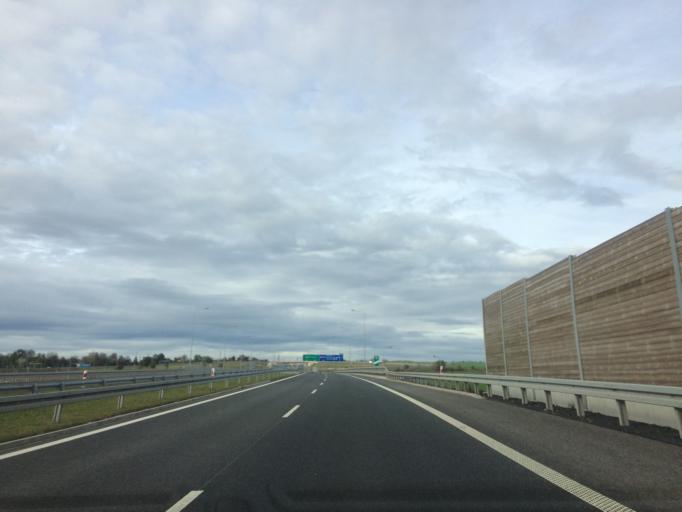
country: PL
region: Lower Silesian Voivodeship
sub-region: Legnica
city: Legnica
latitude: 51.1666
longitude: 16.1009
